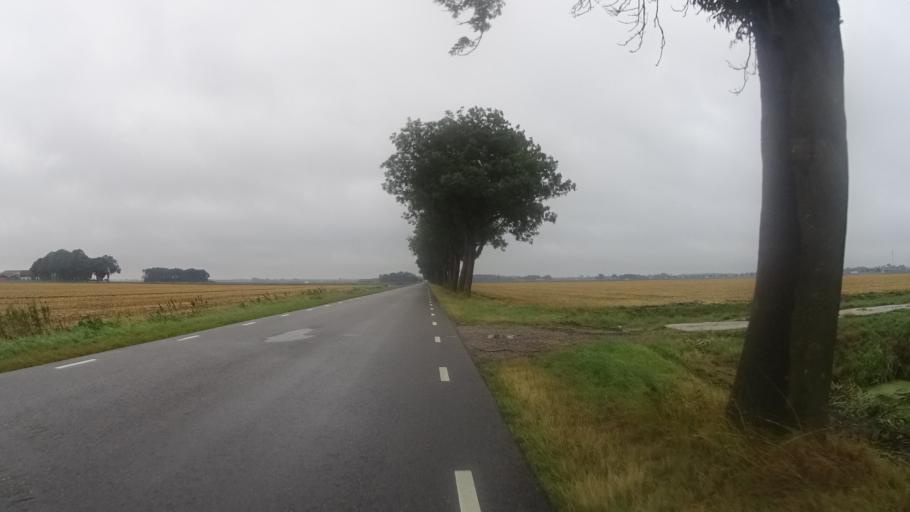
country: NL
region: Groningen
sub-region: Gemeente Veendam
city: Veendam
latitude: 53.1898
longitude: 6.9274
